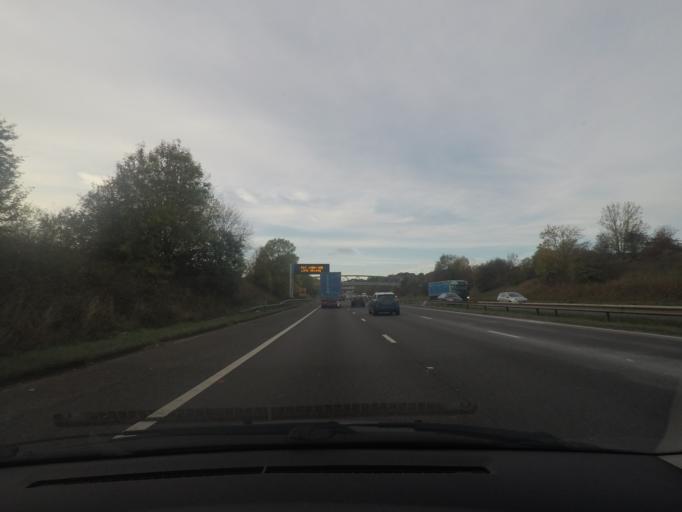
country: GB
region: England
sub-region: Barnsley
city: Stainborough
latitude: 53.5319
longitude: -1.4994
